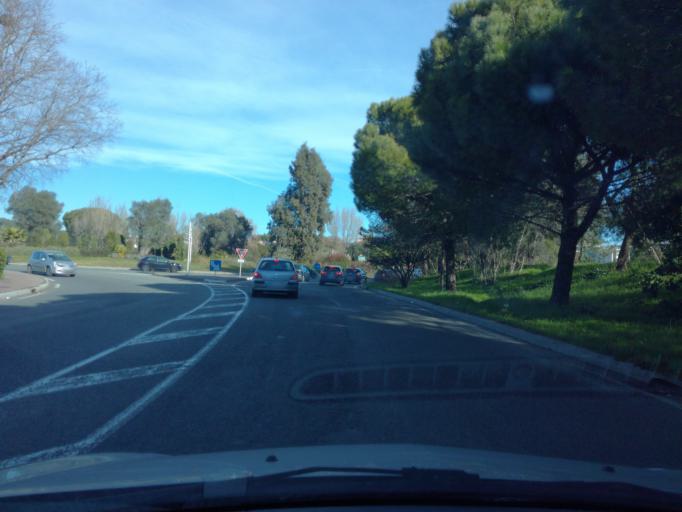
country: FR
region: Provence-Alpes-Cote d'Azur
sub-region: Departement des Alpes-Maritimes
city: Vallauris
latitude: 43.5777
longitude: 7.0905
